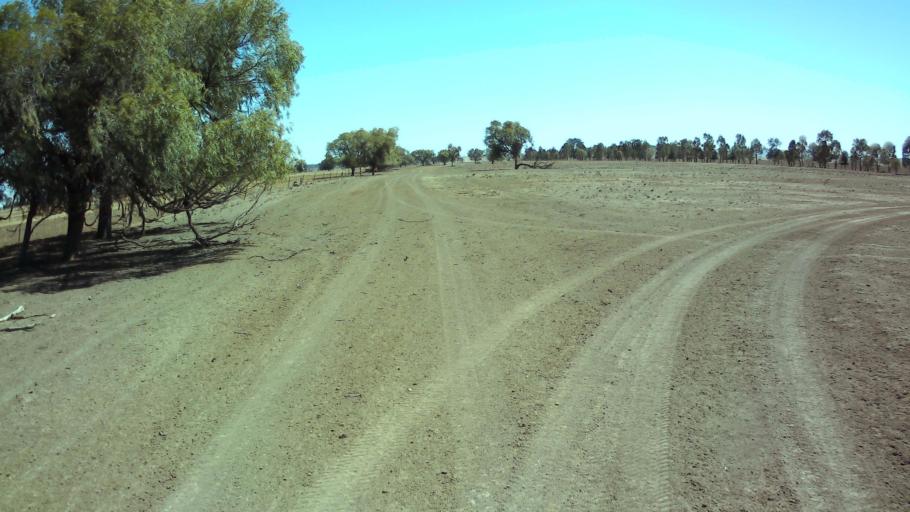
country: AU
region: New South Wales
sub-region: Forbes
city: Forbes
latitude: -33.7189
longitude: 147.6660
